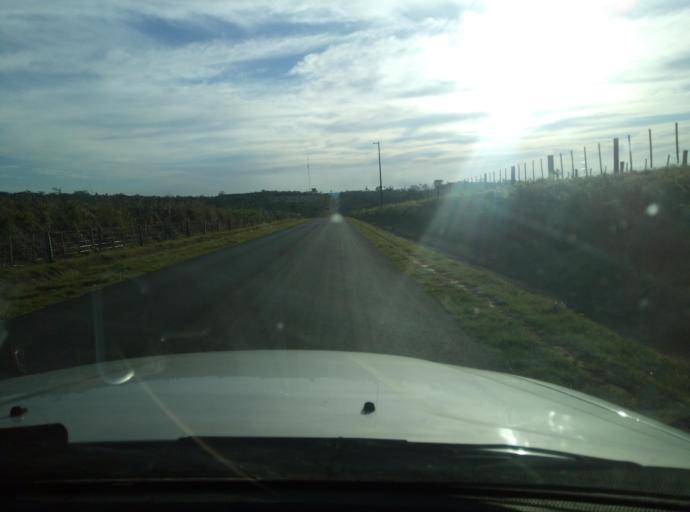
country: PY
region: Caaguazu
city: Carayao
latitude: -25.1546
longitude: -56.3153
